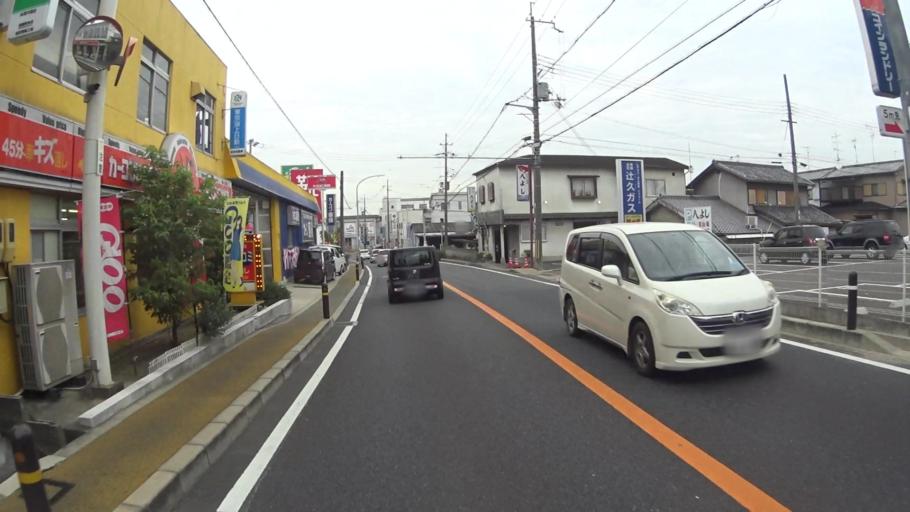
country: JP
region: Kyoto
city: Tanabe
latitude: 34.8591
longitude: 135.7765
